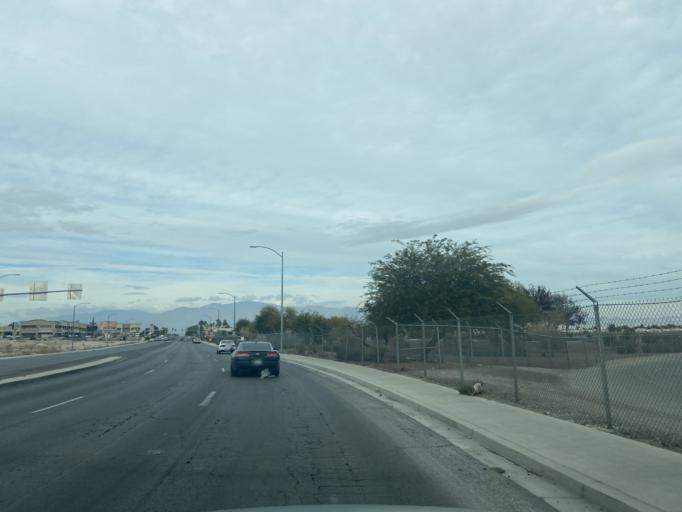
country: US
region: Nevada
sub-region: Clark County
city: Las Vegas
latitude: 36.2142
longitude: -115.2074
